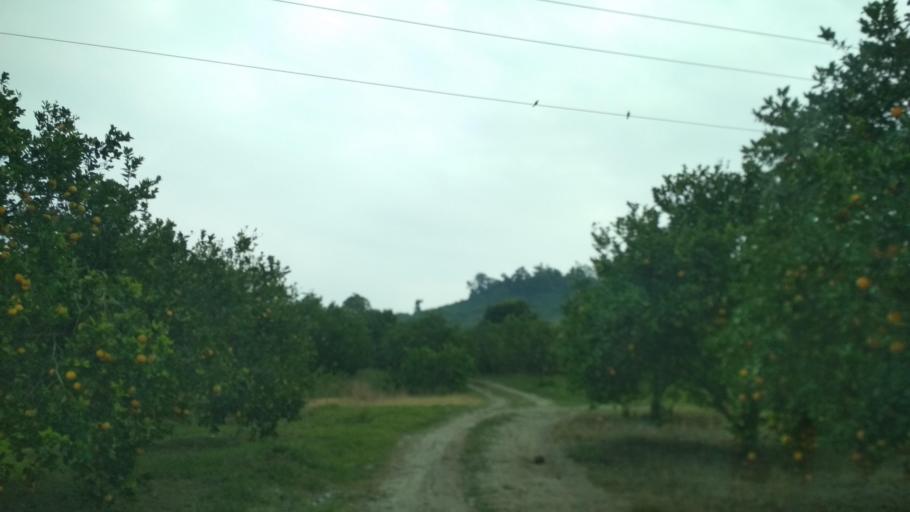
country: MM
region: Kayah
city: Loikaw
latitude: 20.2141
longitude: 97.3290
